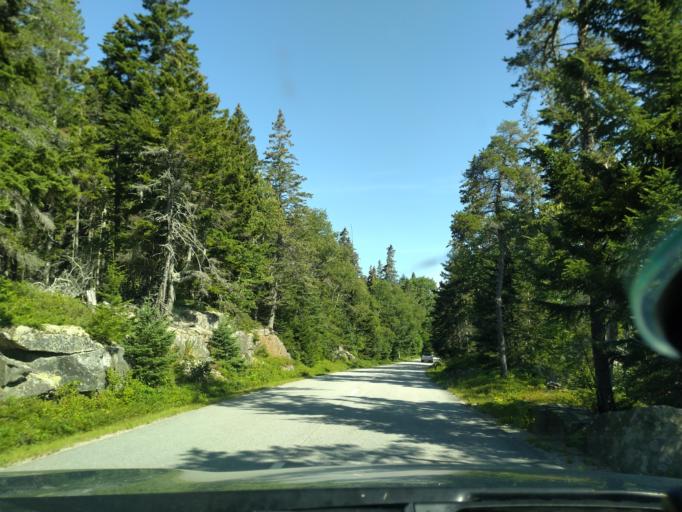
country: US
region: Maine
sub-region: Hancock County
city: Gouldsboro
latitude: 44.3522
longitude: -68.0472
